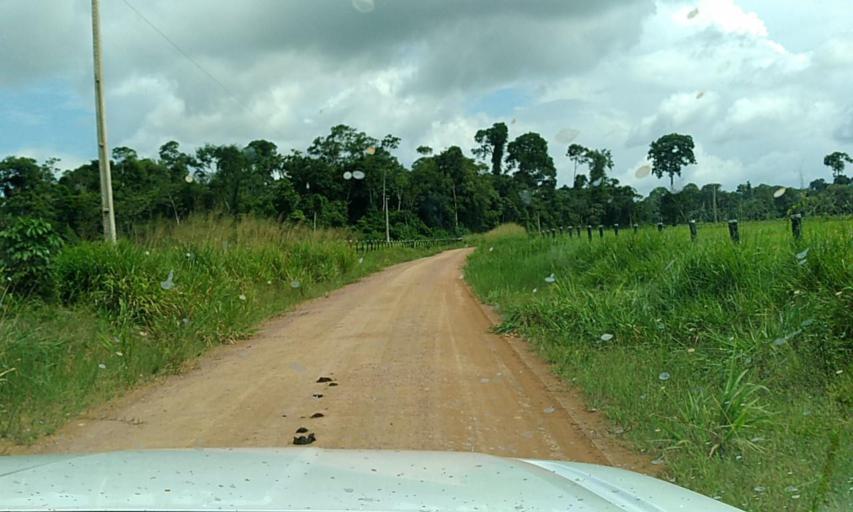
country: BR
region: Para
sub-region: Senador Jose Porfirio
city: Senador Jose Porfirio
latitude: -2.5155
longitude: -51.8397
